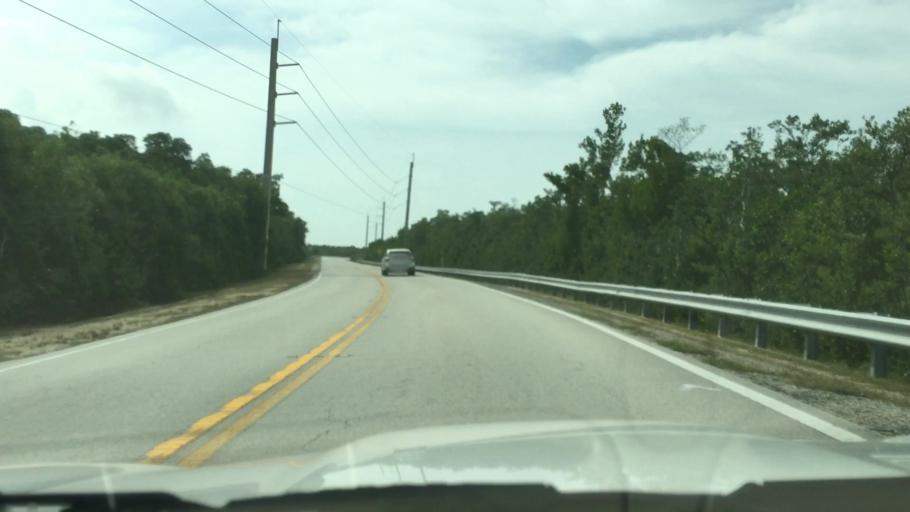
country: US
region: Florida
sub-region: Monroe County
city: North Key Largo
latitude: 25.2828
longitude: -80.3362
